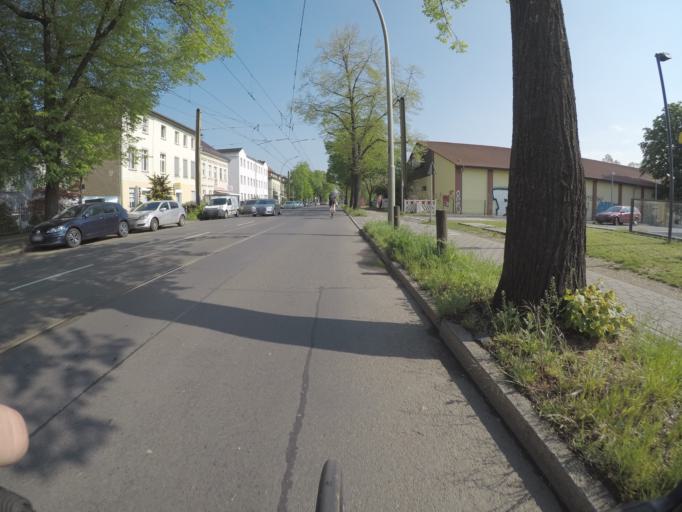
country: DE
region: Berlin
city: Buchholz
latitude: 52.6037
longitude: 13.4319
